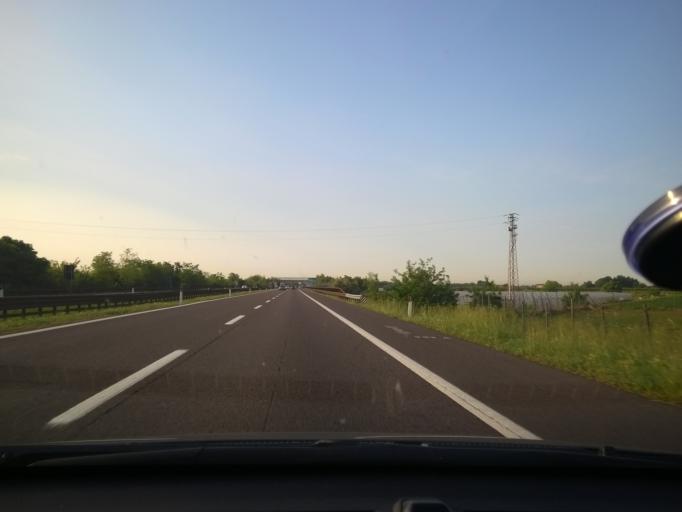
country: IT
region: Veneto
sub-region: Provincia di Verona
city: Alpo
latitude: 45.3682
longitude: 10.9182
